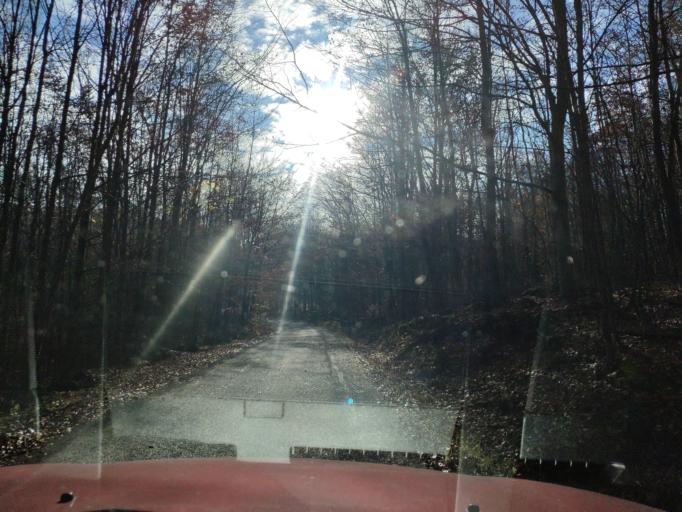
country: HU
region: Borsod-Abauj-Zemplen
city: Gonc
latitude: 48.6025
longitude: 21.4513
